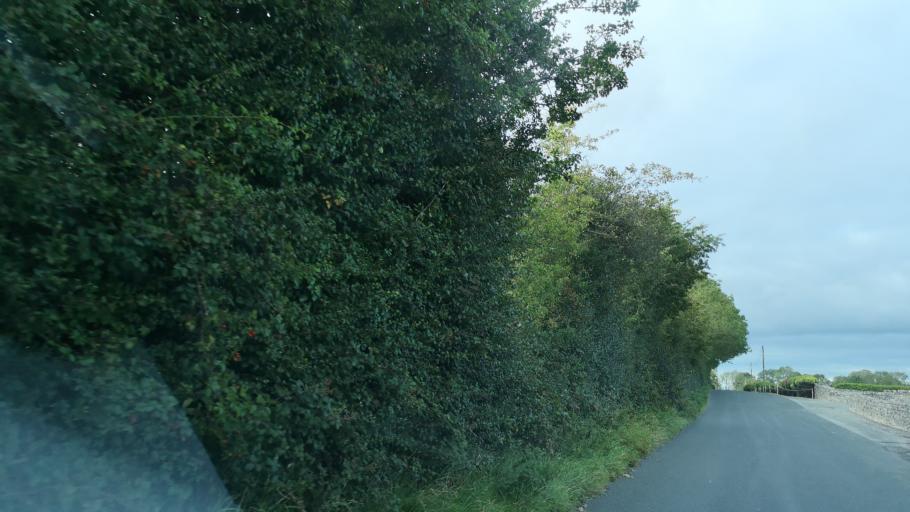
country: IE
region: Connaught
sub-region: County Galway
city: Ballinasloe
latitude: 53.3288
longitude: -8.0979
